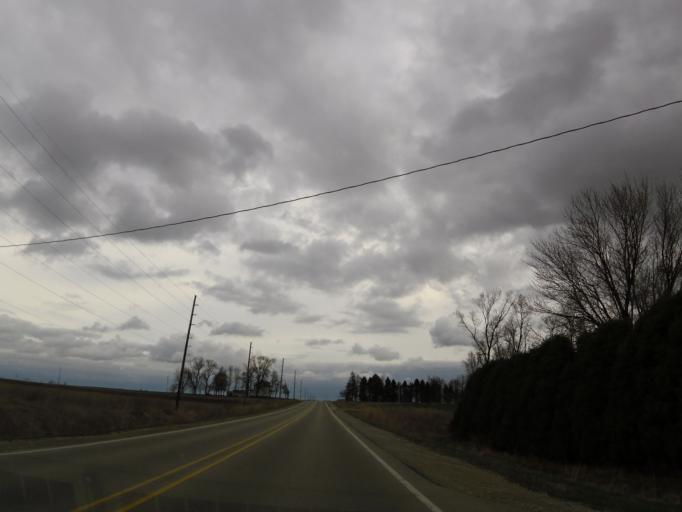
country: US
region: Iowa
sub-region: Black Hawk County
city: Elk Run Heights
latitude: 42.5148
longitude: -92.2195
